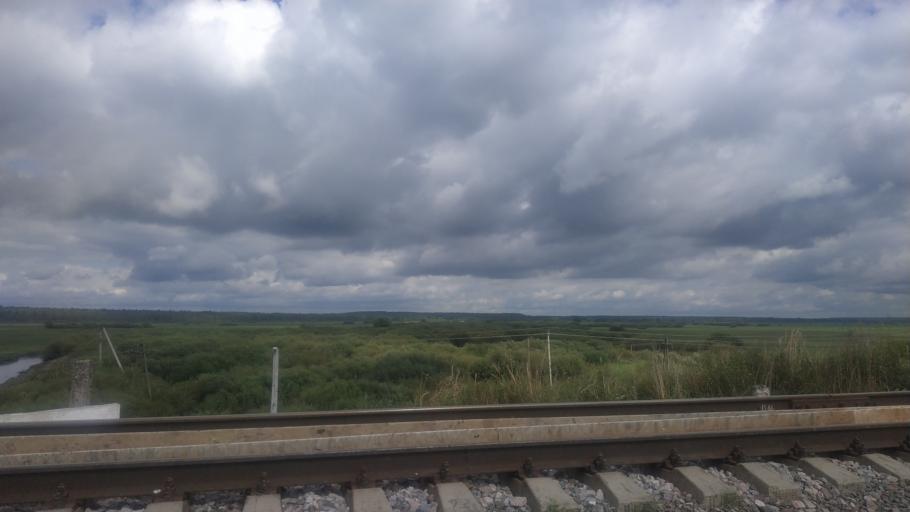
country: RU
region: Brjansk
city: Zhukovka
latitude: 53.5619
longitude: 33.7055
